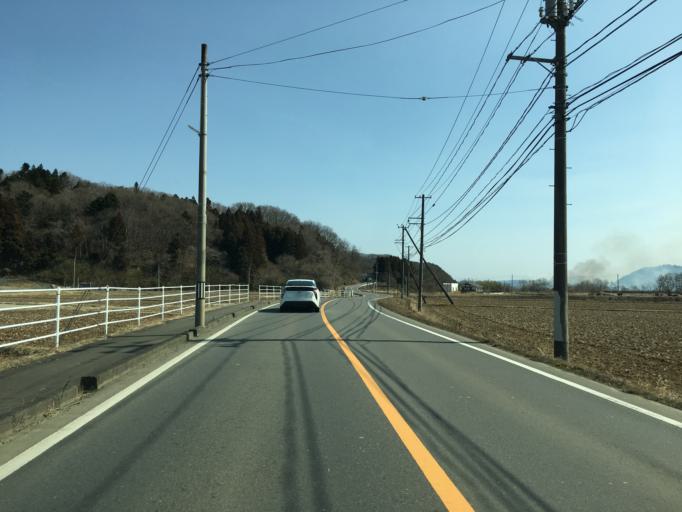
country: JP
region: Fukushima
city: Ishikawa
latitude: 37.1320
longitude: 140.2818
